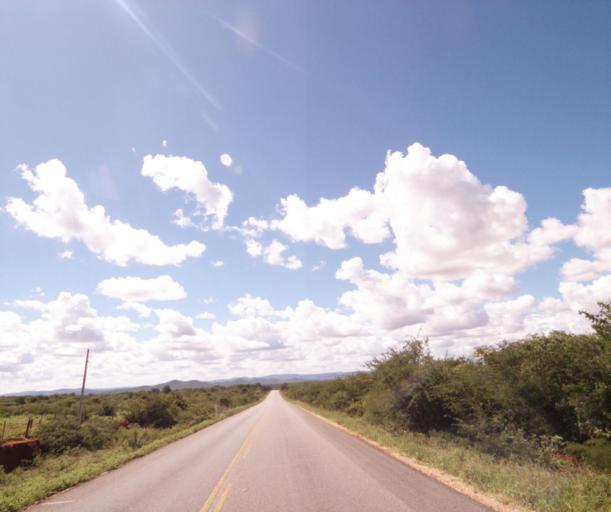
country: BR
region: Bahia
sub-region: Cacule
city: Cacule
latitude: -14.1862
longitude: -42.1618
